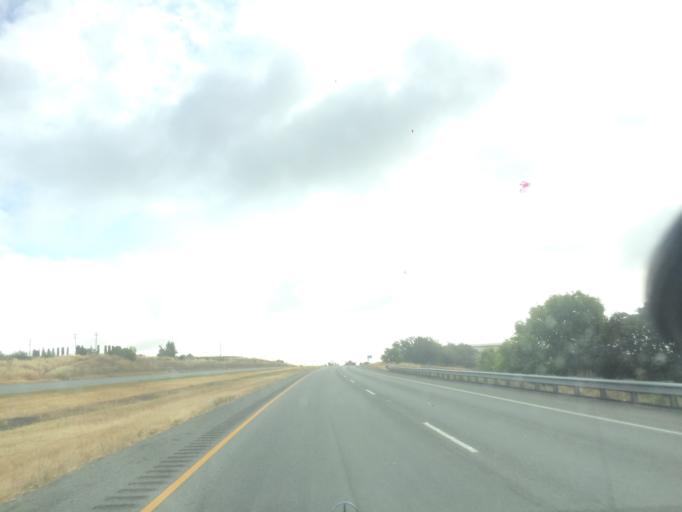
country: US
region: California
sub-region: San Luis Obispo County
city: Paso Robles
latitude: 35.6581
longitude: -120.6079
